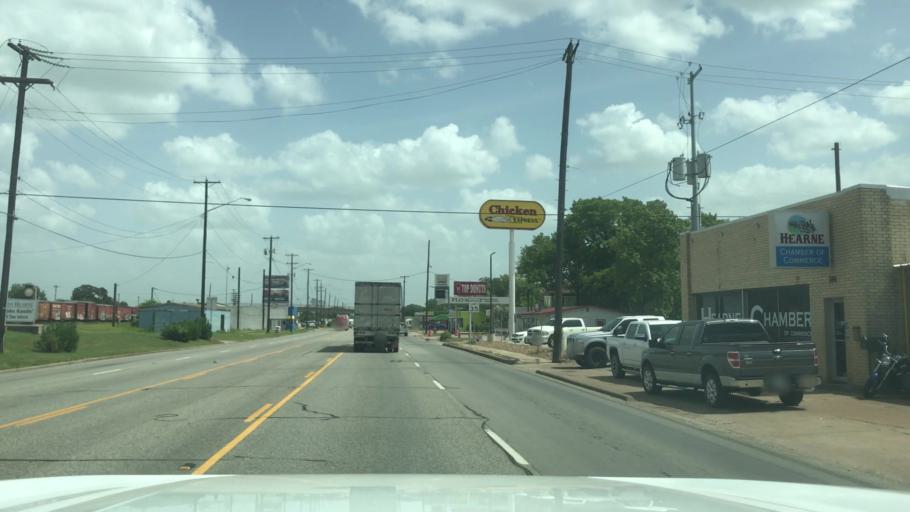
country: US
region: Texas
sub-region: Robertson County
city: Hearne
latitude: 30.8809
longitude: -96.5947
